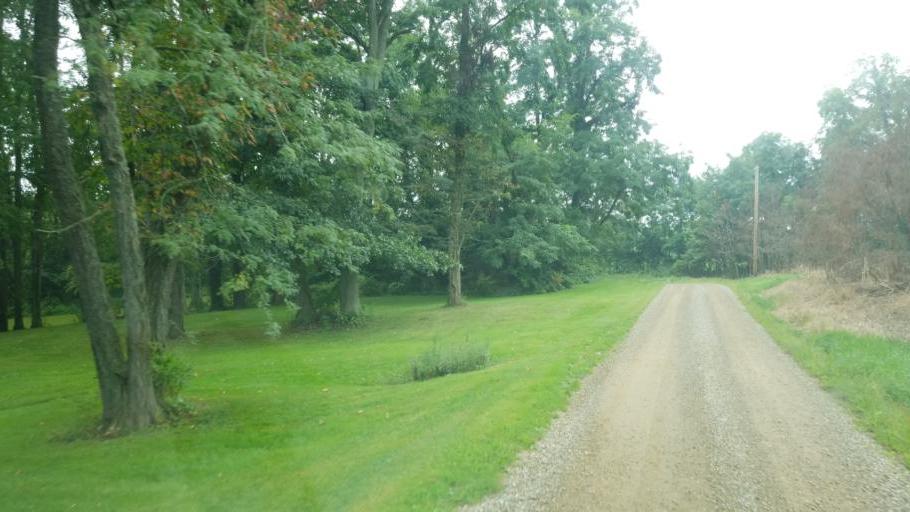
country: US
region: Ohio
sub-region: Licking County
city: Utica
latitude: 40.2739
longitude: -82.4019
